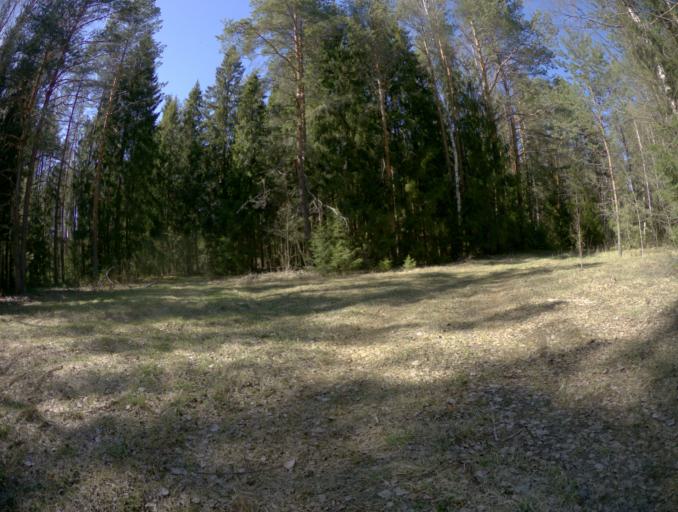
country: RU
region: Vladimir
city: Ivanishchi
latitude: 55.8400
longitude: 40.4376
